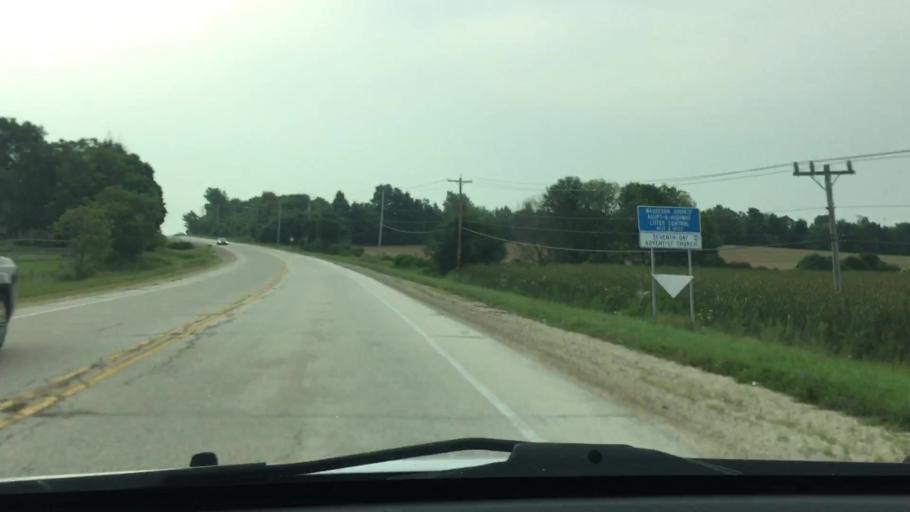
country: US
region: Wisconsin
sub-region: Waukesha County
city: Waukesha
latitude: 42.9944
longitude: -88.1753
